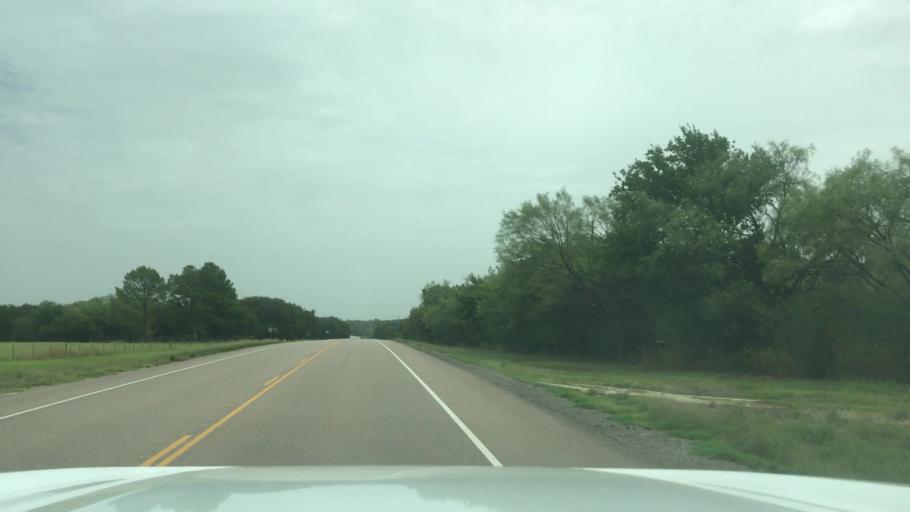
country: US
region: Texas
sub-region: Hamilton County
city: Hico
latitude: 31.9775
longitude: -97.8930
